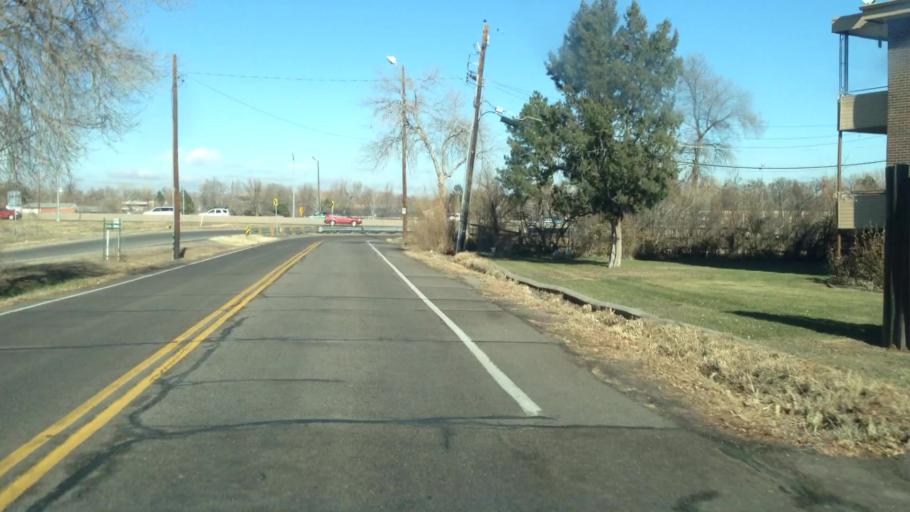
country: US
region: Colorado
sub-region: Jefferson County
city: Lakewood
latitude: 39.7245
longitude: -105.0801
